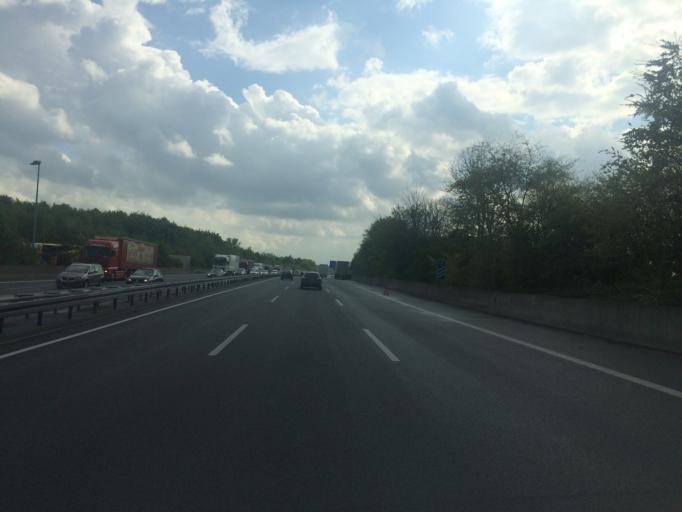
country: DE
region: Lower Saxony
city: Pohle
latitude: 52.2631
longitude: 9.3140
